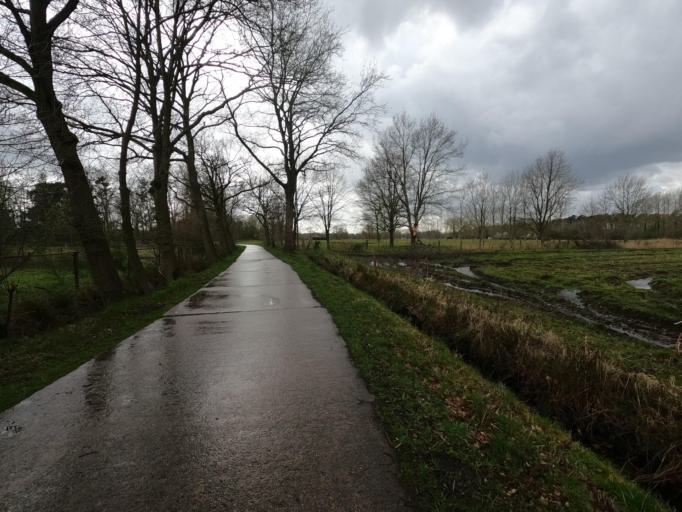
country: BE
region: Flanders
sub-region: Provincie Antwerpen
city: Zandhoven
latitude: 51.2505
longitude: 4.6595
